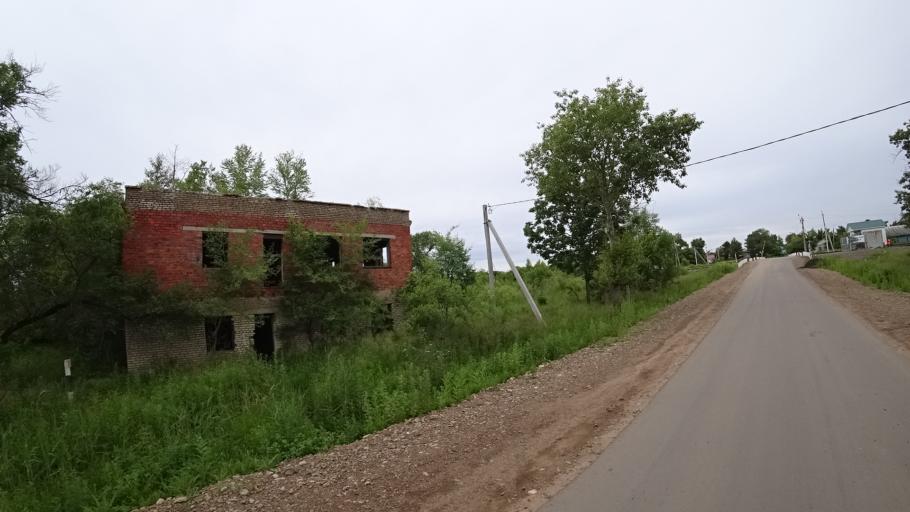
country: RU
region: Primorskiy
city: Novosysoyevka
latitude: 44.2114
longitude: 133.3393
